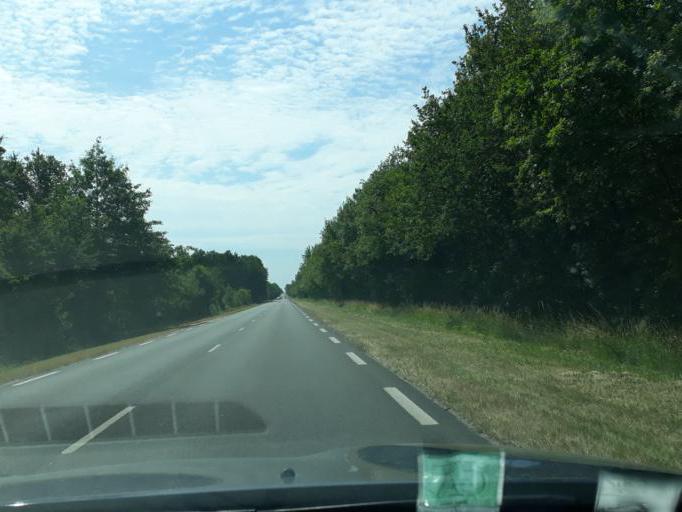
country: FR
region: Centre
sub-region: Departement du Loiret
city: Menestreau-en-Villette
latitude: 47.6638
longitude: 1.9782
